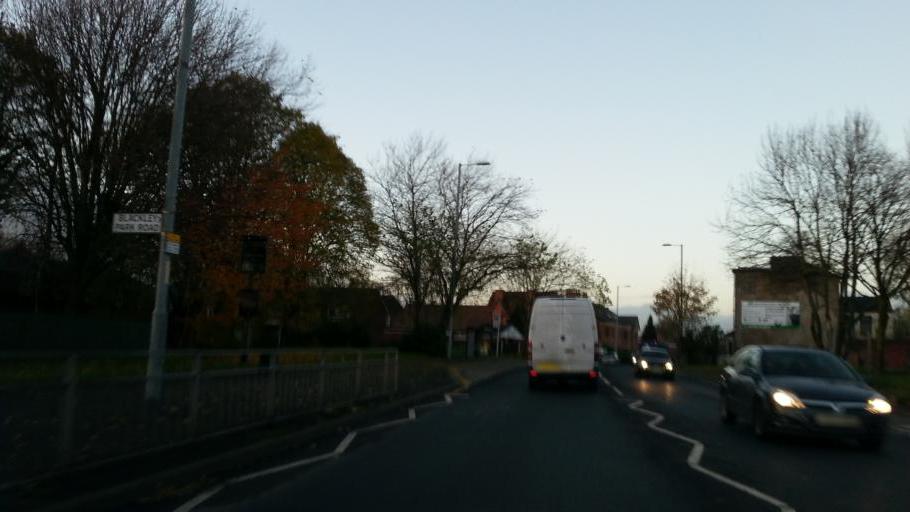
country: GB
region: England
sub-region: Manchester
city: Blackley
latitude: 53.5168
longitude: -2.2131
